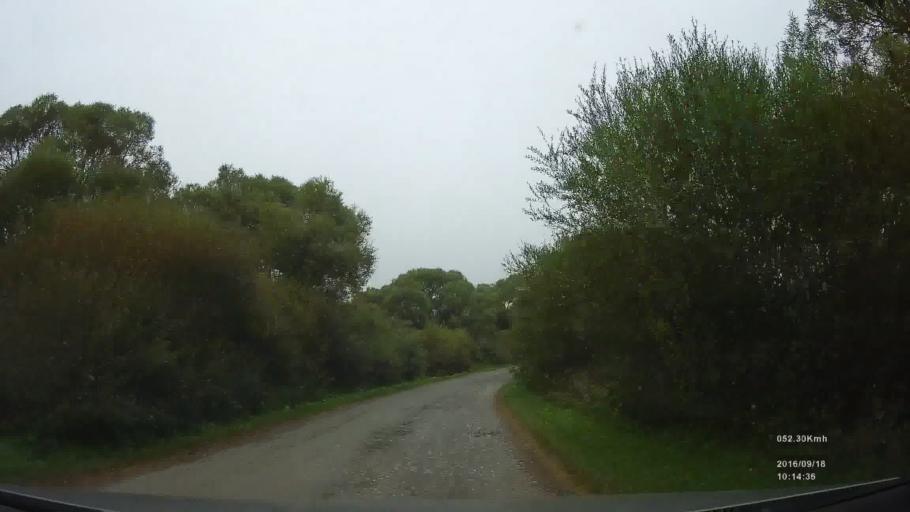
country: SK
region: Kosicky
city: Spisska Nova Ves
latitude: 48.9413
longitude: 20.6252
